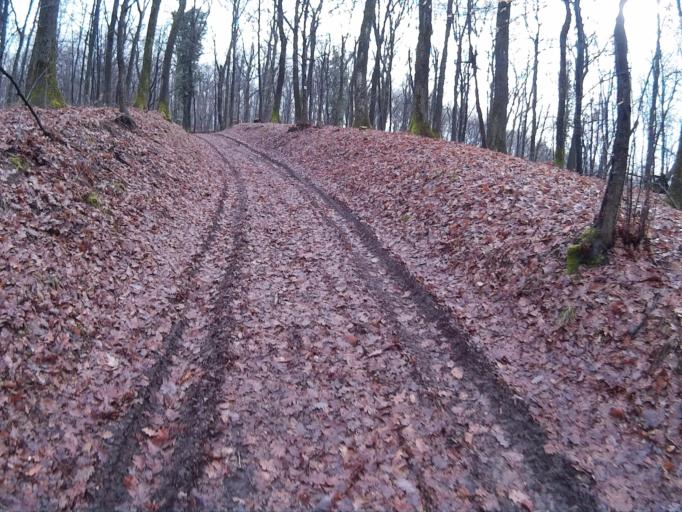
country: HU
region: Borsod-Abauj-Zemplen
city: Satoraljaujhely
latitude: 48.4166
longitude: 21.5848
